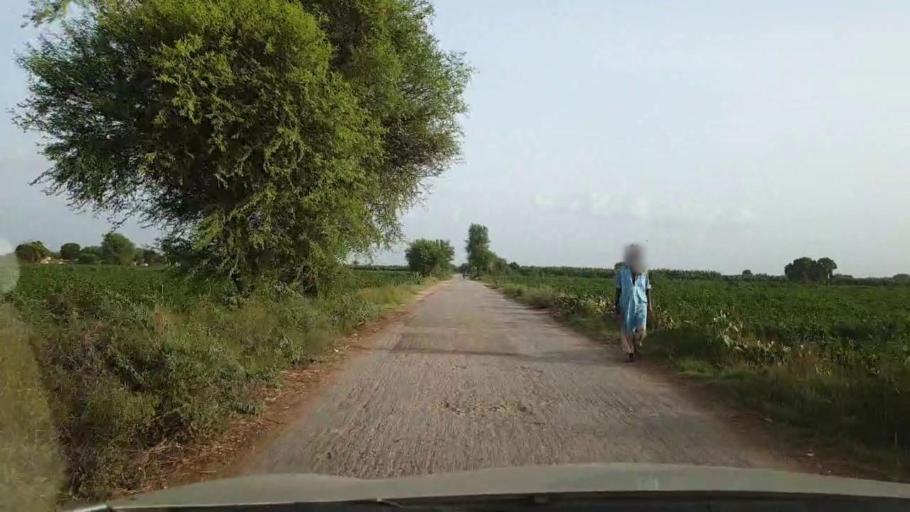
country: PK
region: Sindh
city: Tando Ghulam Ali
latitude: 25.1046
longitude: 68.8848
